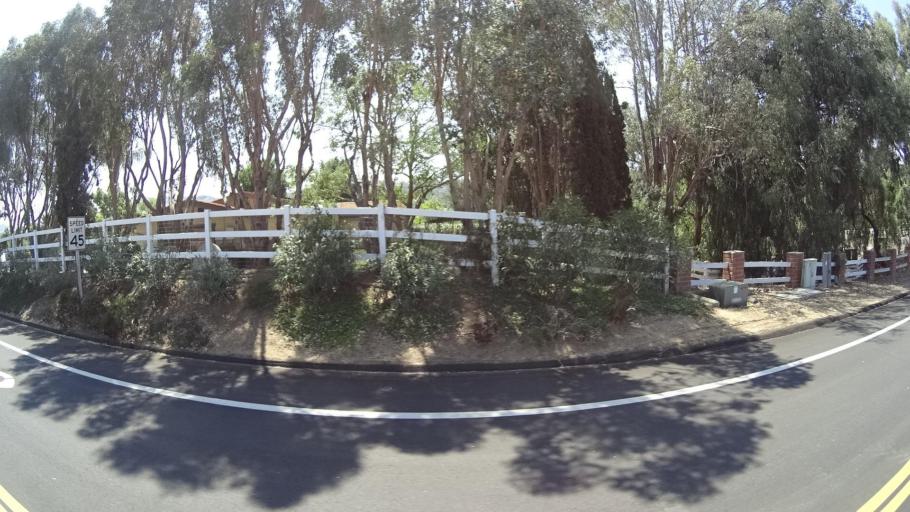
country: US
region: California
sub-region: San Diego County
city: Bonsall
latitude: 33.2820
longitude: -117.1918
